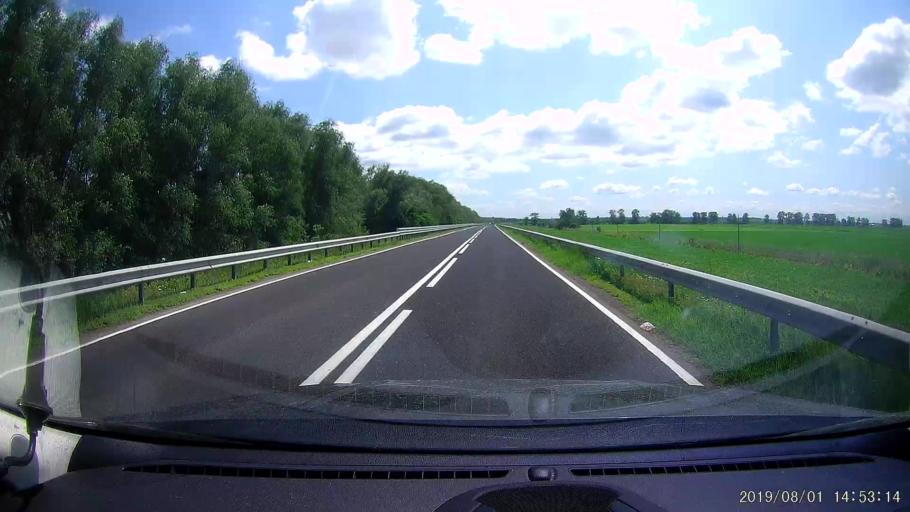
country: RO
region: Braila
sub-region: Municipiul Braila
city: Braila
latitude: 45.3401
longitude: 28.0055
